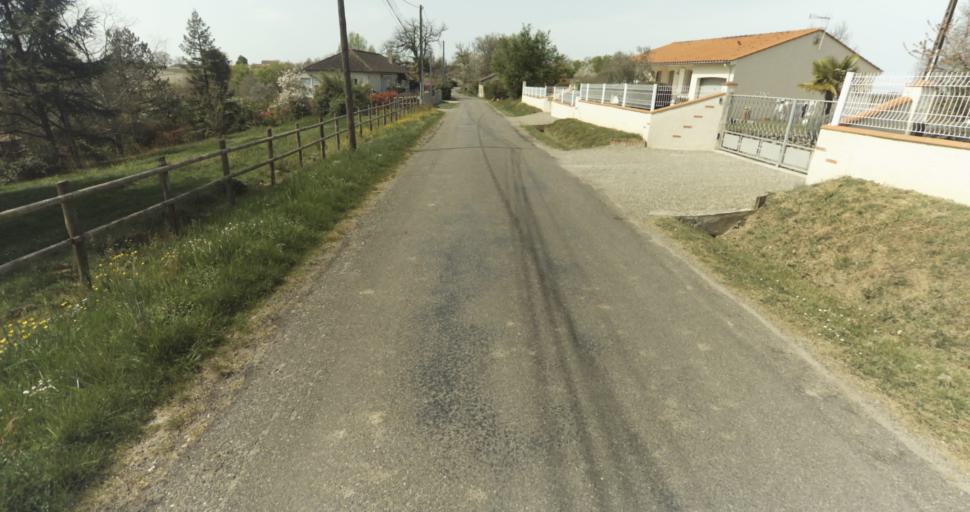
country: FR
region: Midi-Pyrenees
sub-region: Departement du Tarn-et-Garonne
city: Moissac
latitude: 44.1315
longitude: 1.0767
